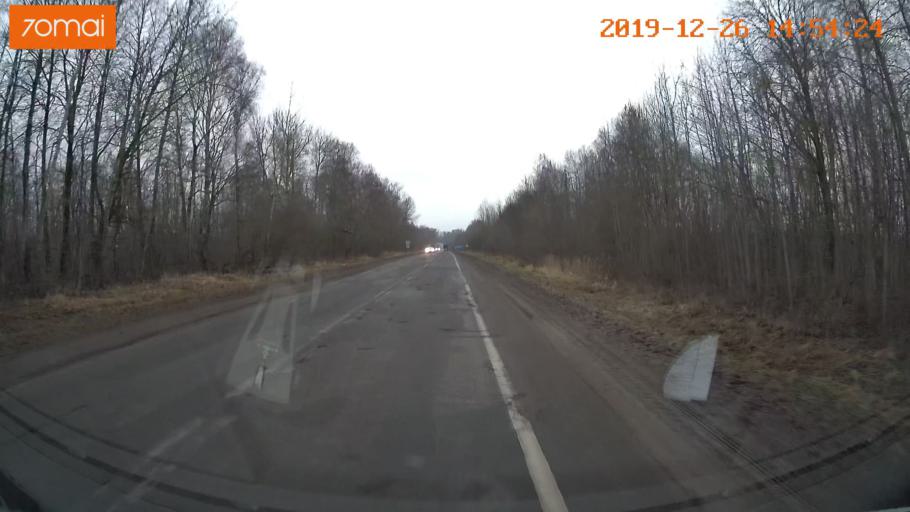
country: RU
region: Jaroslavl
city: Rybinsk
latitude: 58.3075
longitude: 38.8847
